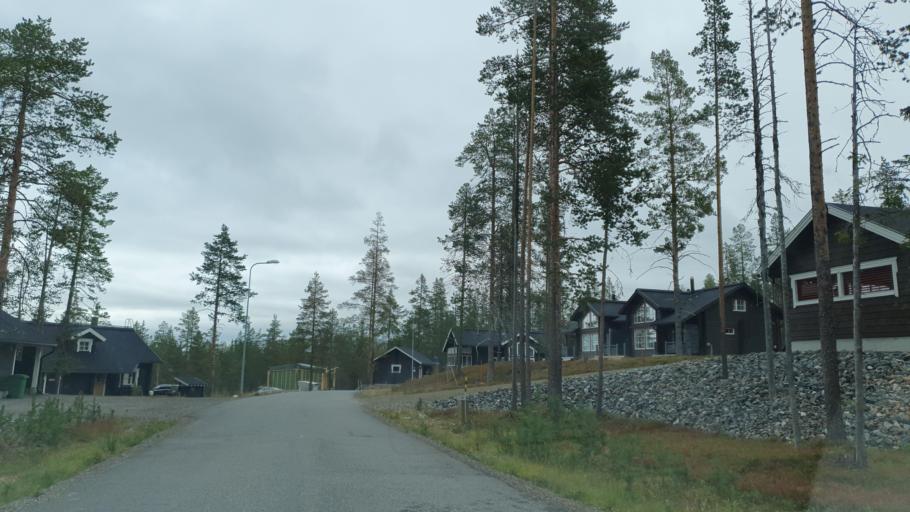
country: FI
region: Lapland
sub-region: Tunturi-Lappi
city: Kolari
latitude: 67.5928
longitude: 24.1772
